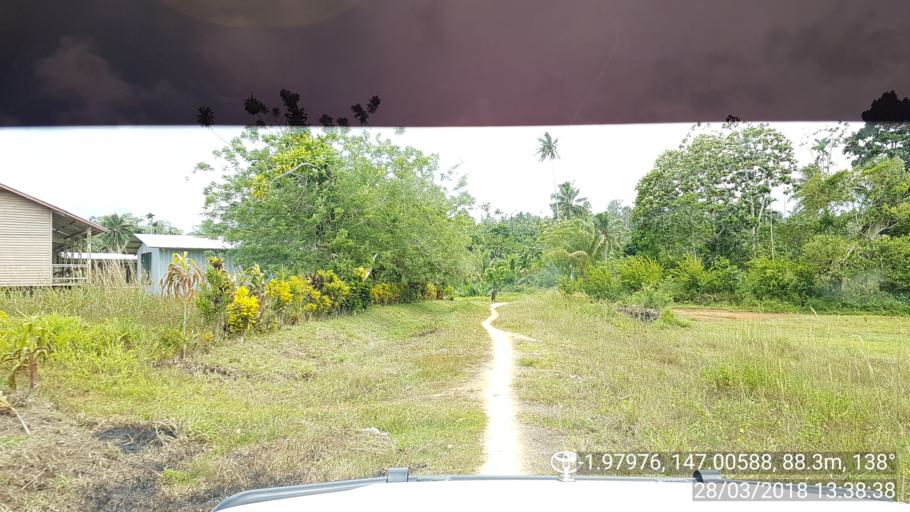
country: PG
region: Manus
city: Lorengau
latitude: -1.9802
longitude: 147.0061
